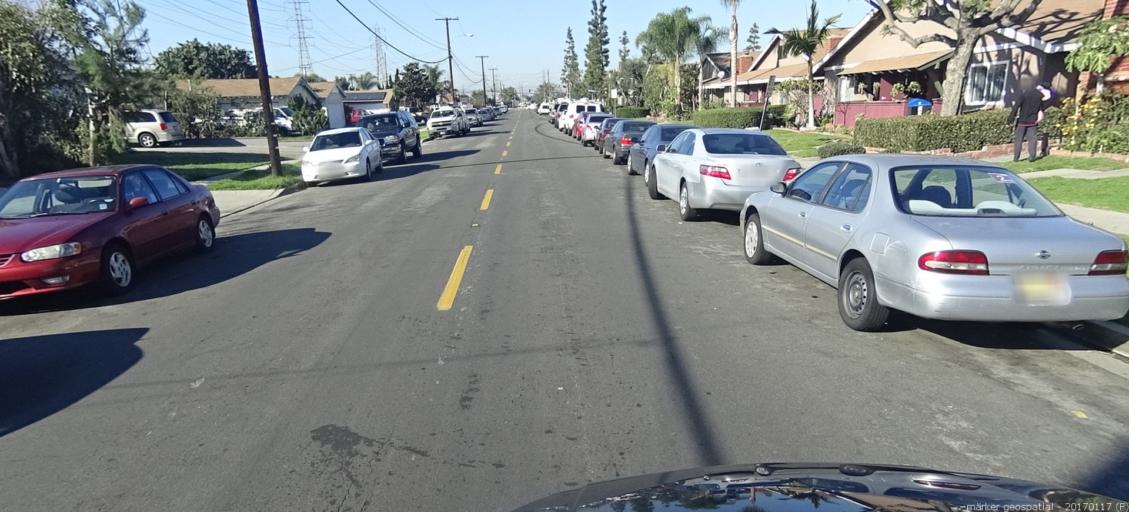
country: US
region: California
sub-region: Orange County
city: Stanton
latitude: 33.8077
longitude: -117.9727
